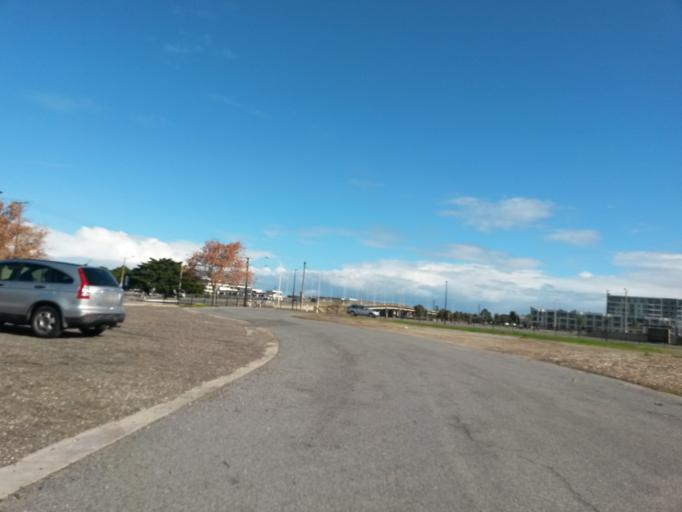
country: AU
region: South Australia
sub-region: Port Adelaide Enfield
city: Birkenhead
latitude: -34.8450
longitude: 138.4991
